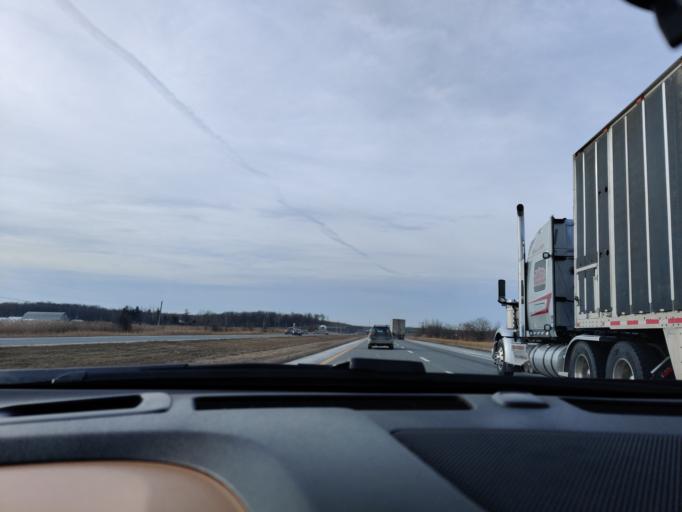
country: CA
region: Quebec
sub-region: Monteregie
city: Saint-Lazare
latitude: 45.3282
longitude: -74.1178
